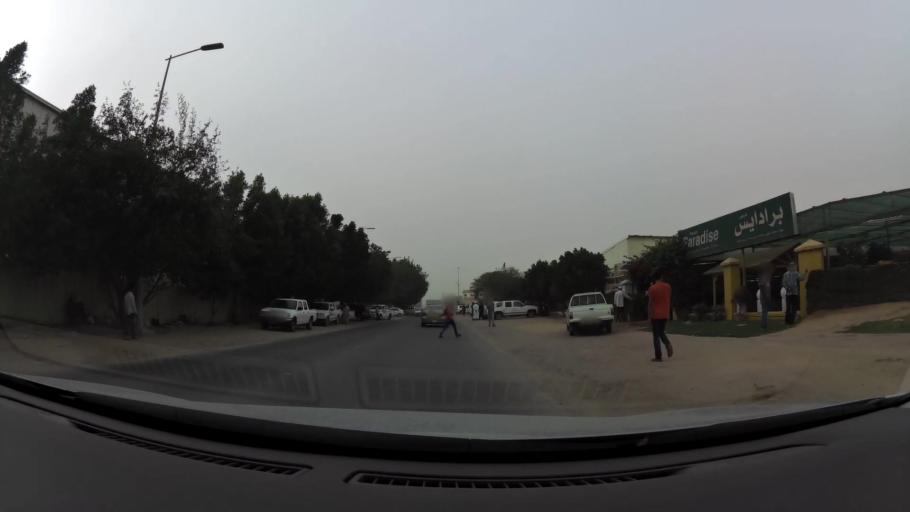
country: QA
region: Baladiyat ad Dawhah
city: Doha
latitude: 25.2489
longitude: 51.4774
